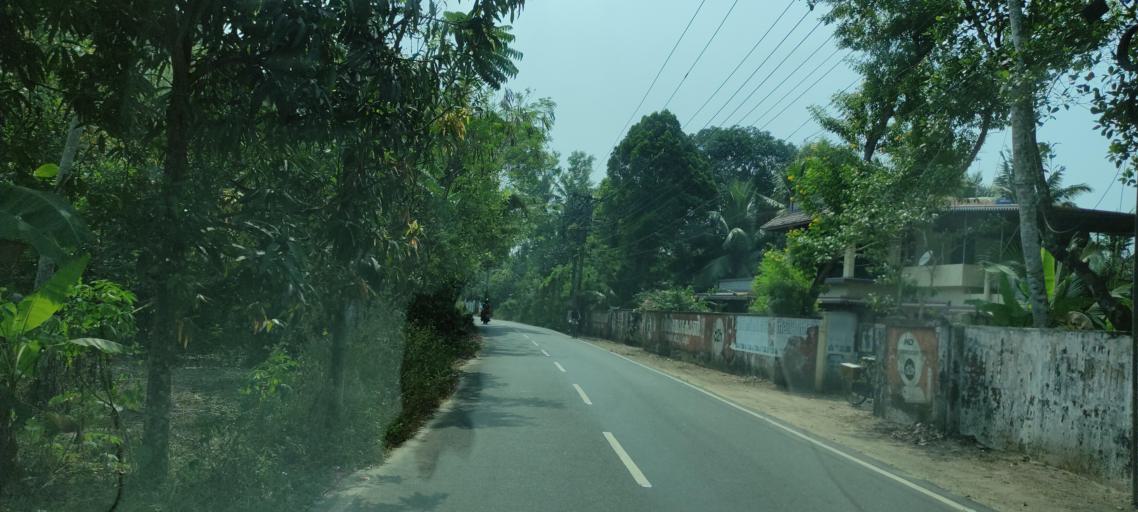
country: IN
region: Kerala
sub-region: Alappuzha
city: Alleppey
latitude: 9.5552
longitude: 76.3336
